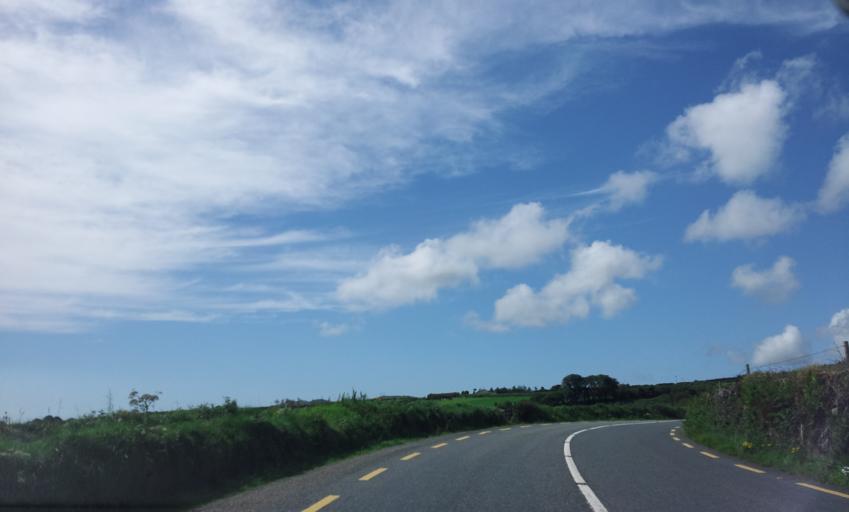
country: IE
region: Munster
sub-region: Ciarrai
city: Dingle
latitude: 52.1438
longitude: -10.0960
